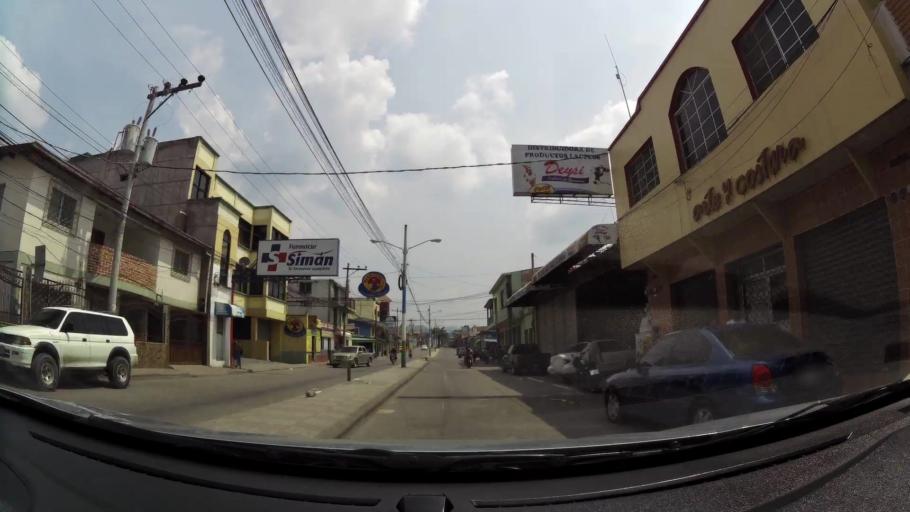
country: HN
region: Comayagua
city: Siguatepeque
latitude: 14.5985
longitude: -87.8313
